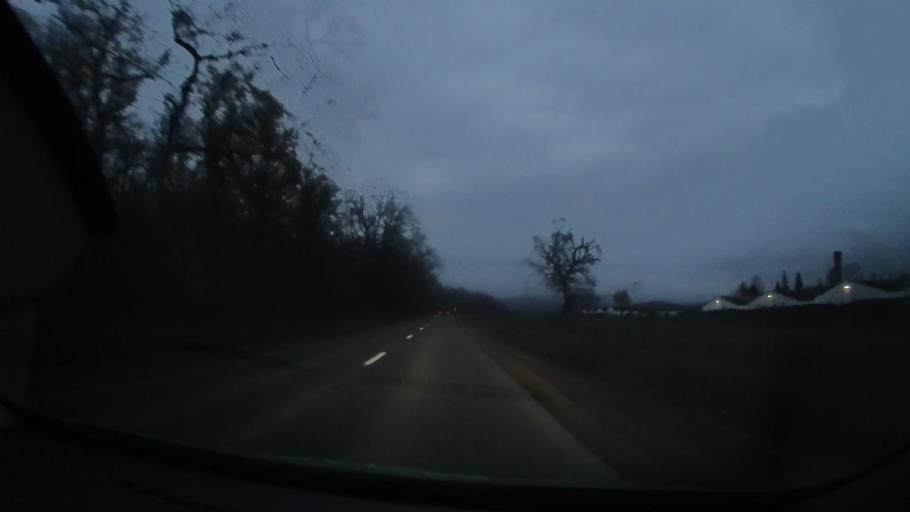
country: RO
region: Mures
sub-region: Comuna Gurghiu
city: Gurghiu
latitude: 46.7714
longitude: 24.8326
